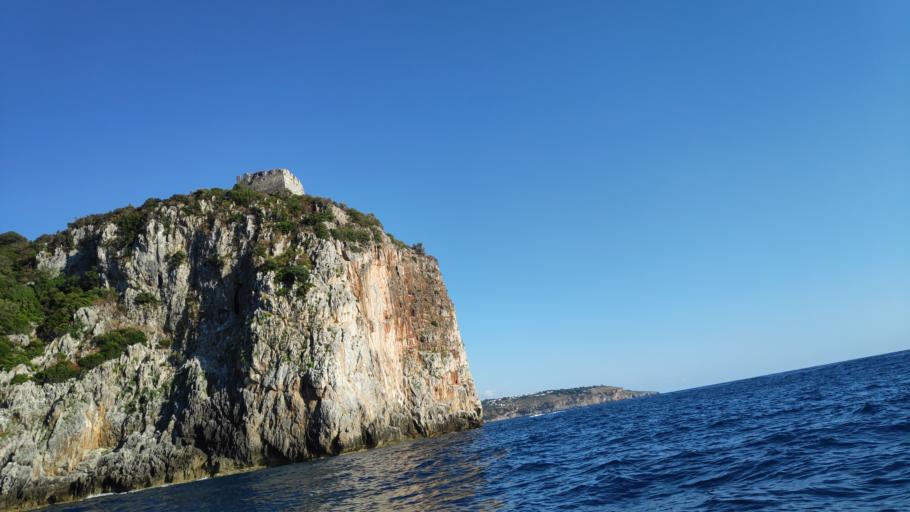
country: IT
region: Calabria
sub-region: Provincia di Cosenza
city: Praia a Mare
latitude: 39.8736
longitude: 15.7683
